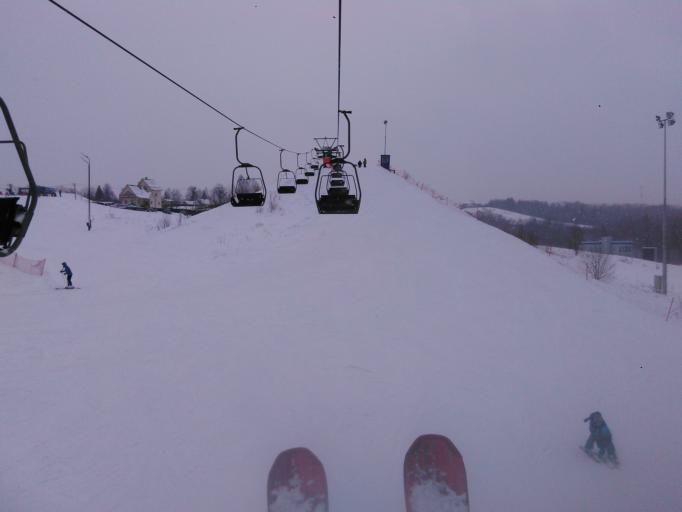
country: RU
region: Moskovskaya
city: Yakhroma
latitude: 56.2516
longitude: 37.4392
